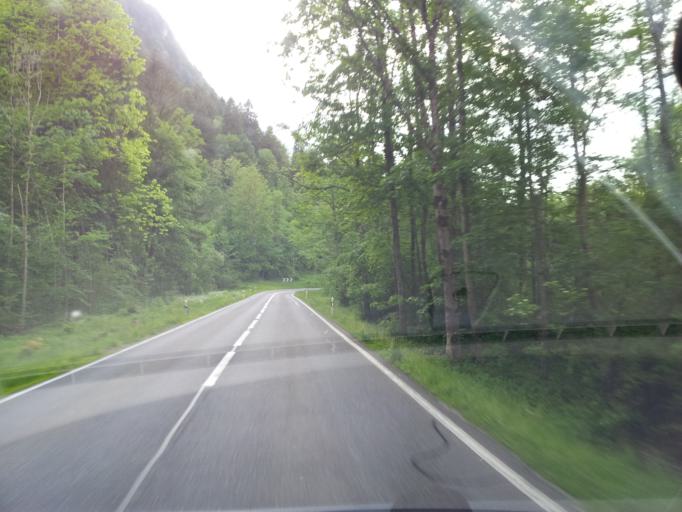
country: CH
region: Bern
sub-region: Interlaken-Oberhasli District
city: Wilderswil
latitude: 46.6371
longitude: 7.8905
